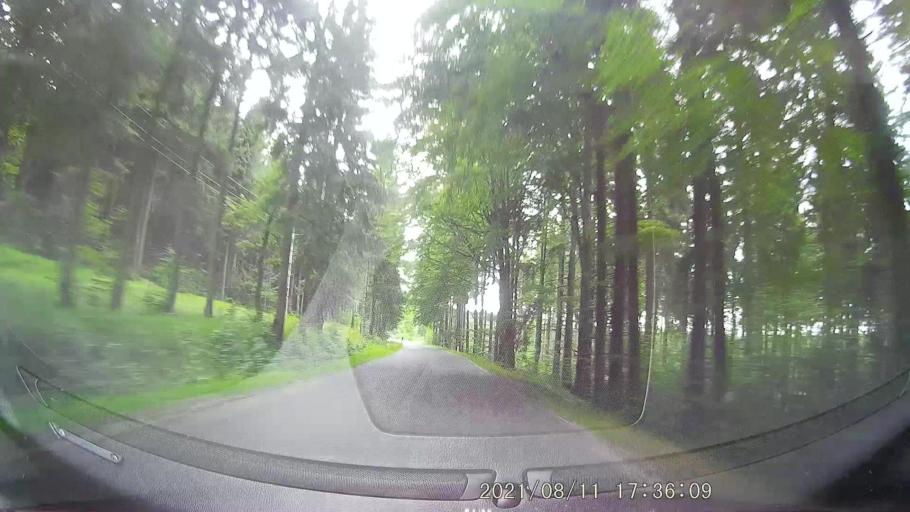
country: PL
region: Lower Silesian Voivodeship
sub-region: Powiat klodzki
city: Duszniki-Zdroj
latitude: 50.3278
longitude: 16.4088
